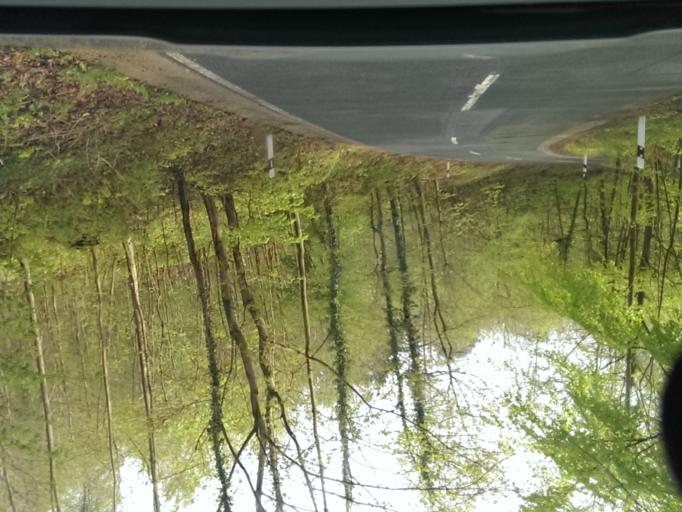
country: DE
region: Lower Saxony
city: Nordstemmen
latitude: 52.1765
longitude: 9.7654
